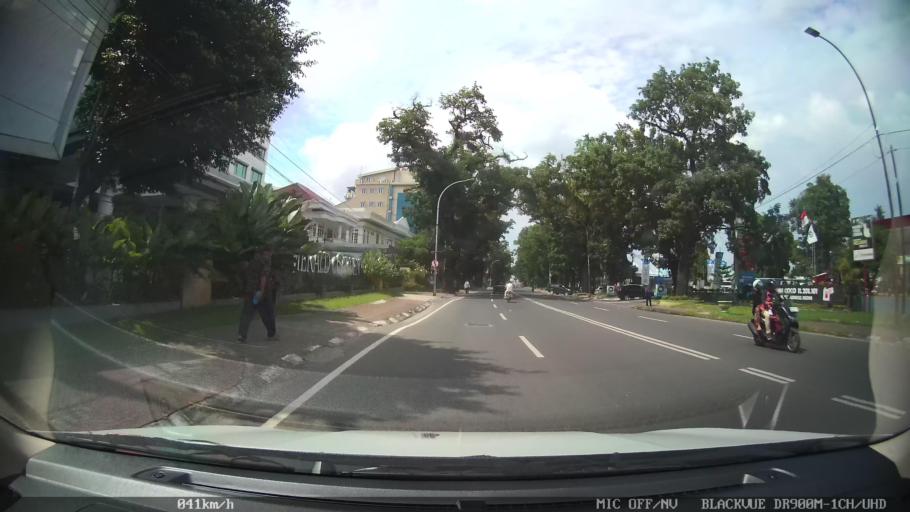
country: ID
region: North Sumatra
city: Medan
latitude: 3.6017
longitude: 98.6732
